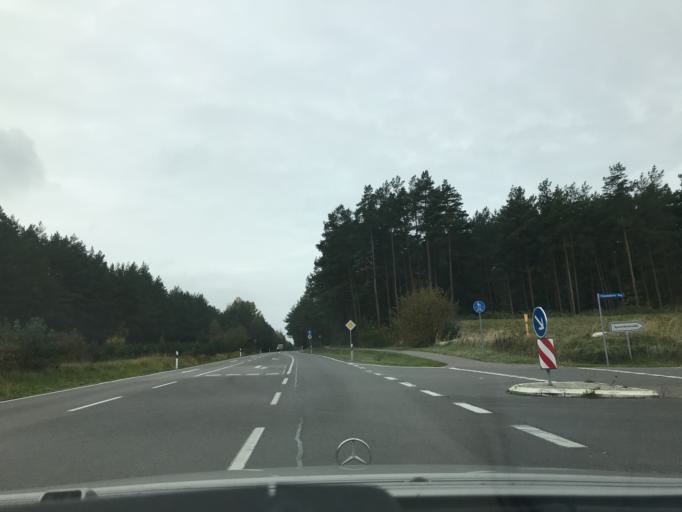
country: DE
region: Mecklenburg-Vorpommern
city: Lubmin
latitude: 54.1371
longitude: 13.6438
